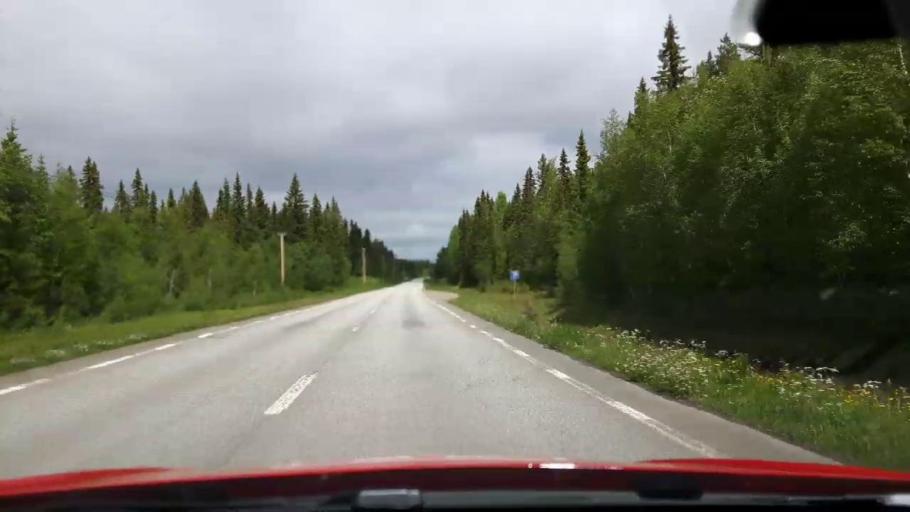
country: SE
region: Jaemtland
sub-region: Krokoms Kommun
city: Krokom
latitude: 63.4864
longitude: 14.5053
